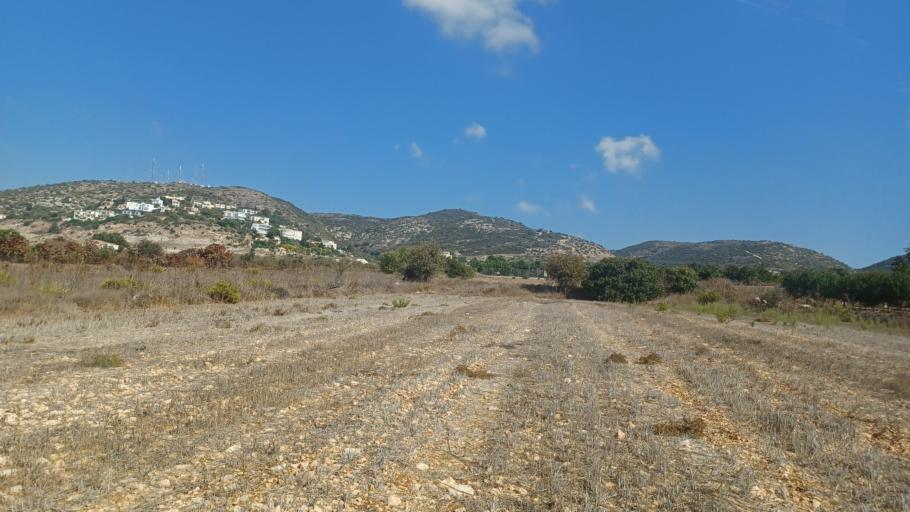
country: CY
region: Pafos
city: Mesogi
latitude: 34.8294
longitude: 32.4518
